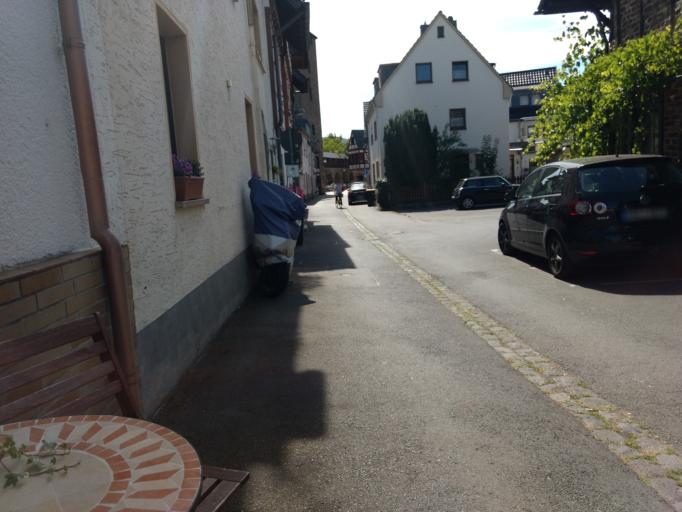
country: DE
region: Rheinland-Pfalz
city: Bad Neuenahr-Ahrweiler
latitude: 50.5412
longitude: 7.0978
